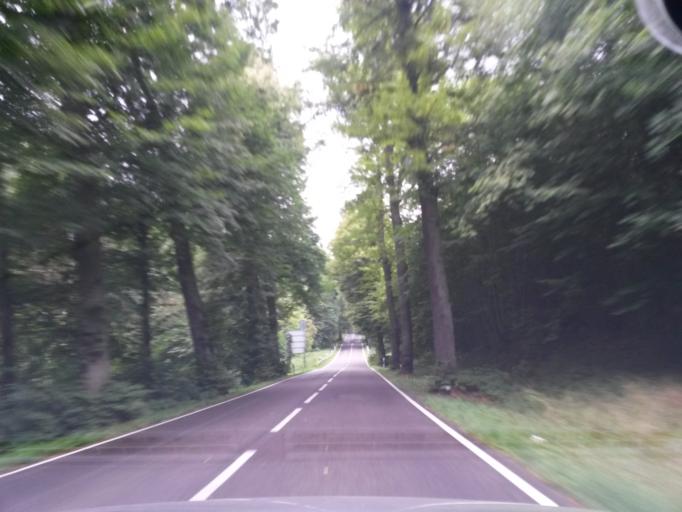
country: DE
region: Brandenburg
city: Gerswalde
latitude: 53.1437
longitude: 13.8625
